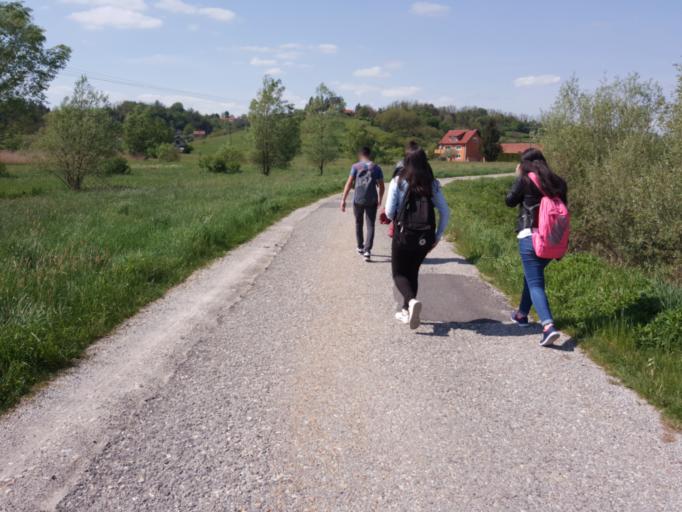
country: HR
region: Varazdinska
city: Lepoglava
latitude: 46.2276
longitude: 15.9657
